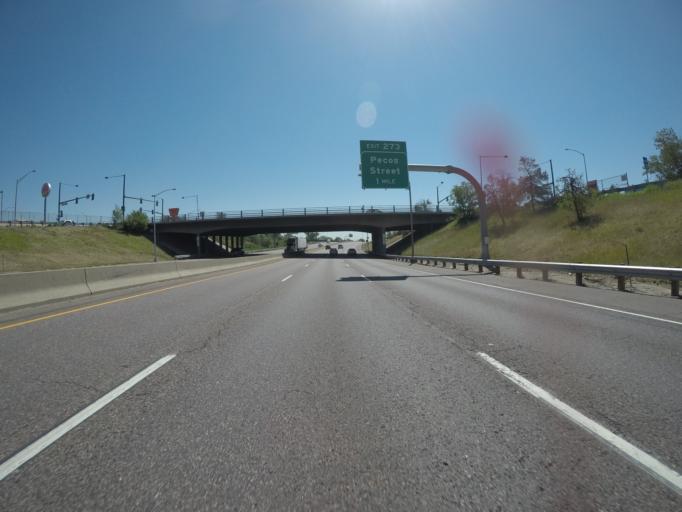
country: US
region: Colorado
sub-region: Adams County
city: Berkley
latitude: 39.7842
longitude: -105.0260
